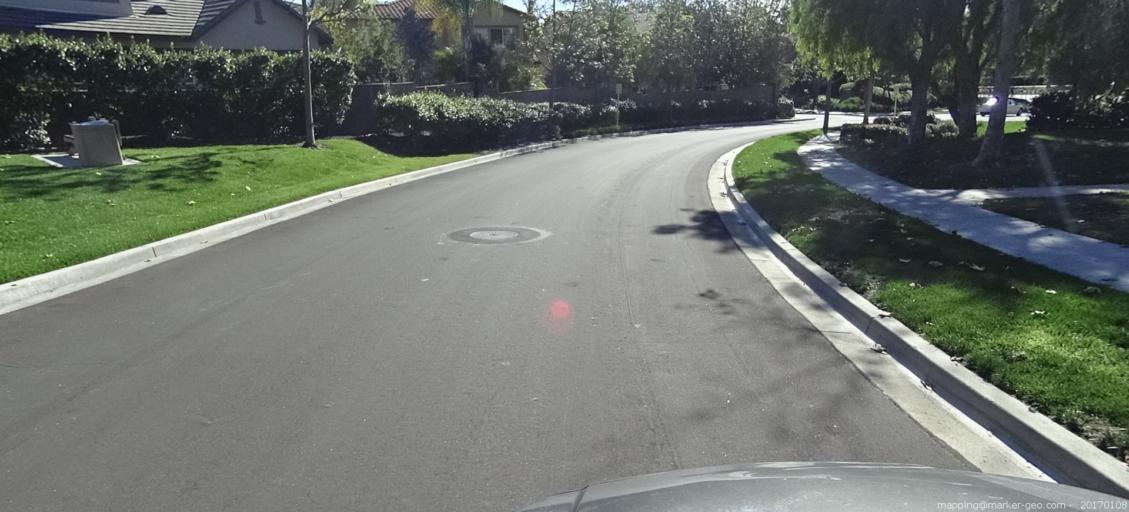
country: US
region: California
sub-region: Orange County
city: Ladera Ranch
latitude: 33.5695
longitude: -117.6316
